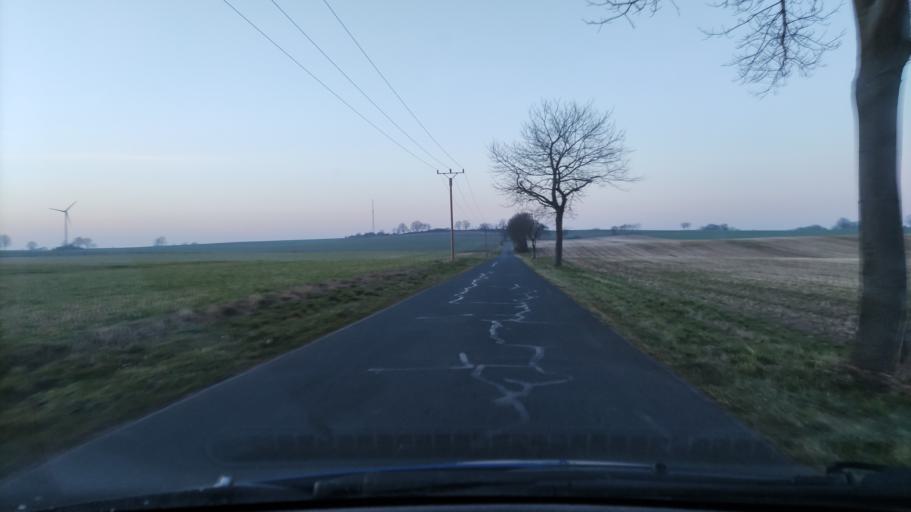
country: DE
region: Lower Saxony
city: Barum
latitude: 53.0423
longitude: 10.4805
